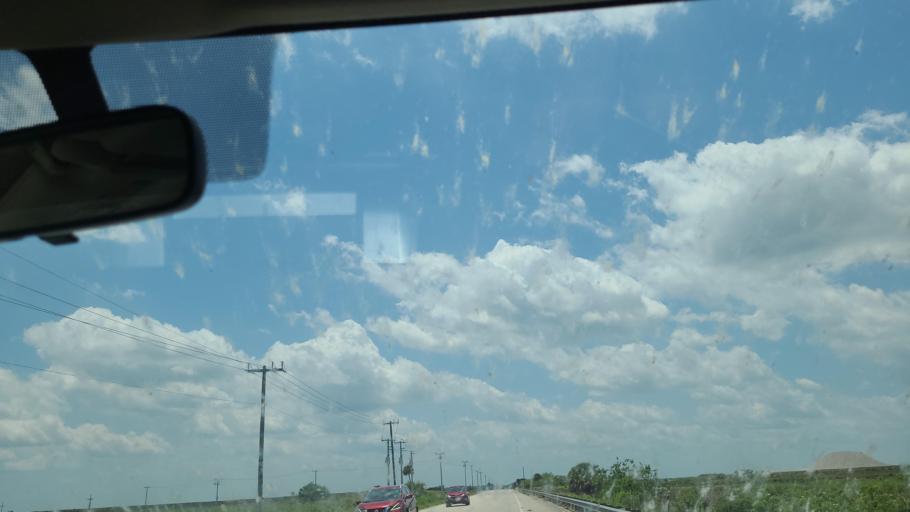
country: US
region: Florida
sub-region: Glades County
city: Buckhead Ridge
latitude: 27.1730
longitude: -81.0940
